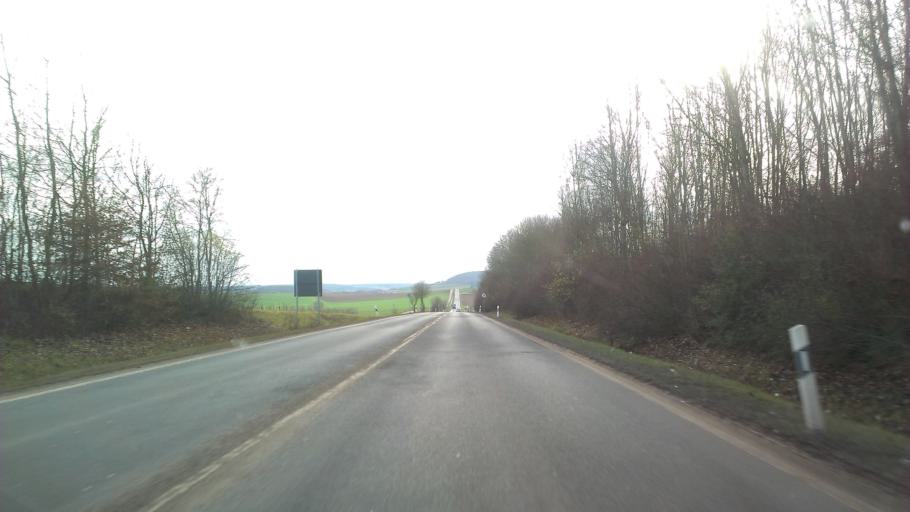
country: DE
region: Rheinland-Pfalz
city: Hackenheim
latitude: 49.8221
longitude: 7.9068
